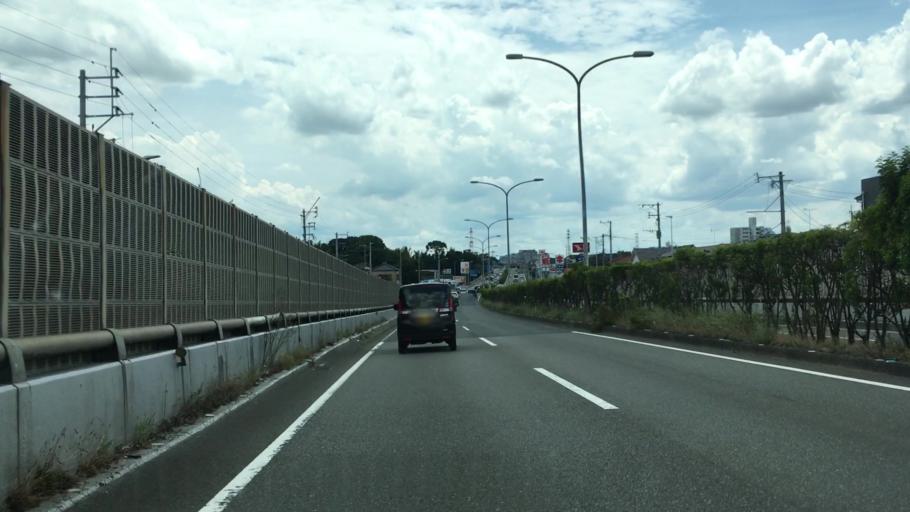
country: JP
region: Fukuoka
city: Chikushino-shi
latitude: 33.4819
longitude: 130.5384
